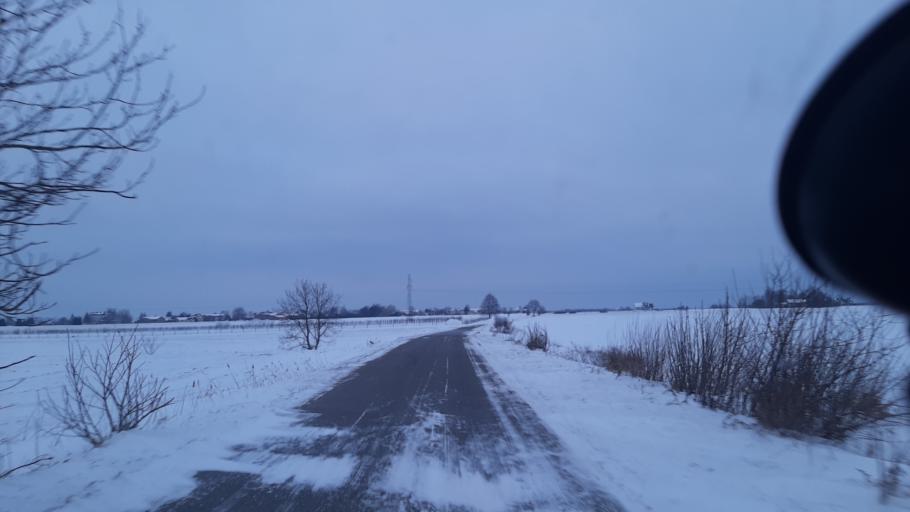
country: PL
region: Lublin Voivodeship
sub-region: Powiat lubelski
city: Jastkow
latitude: 51.3474
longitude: 22.4086
